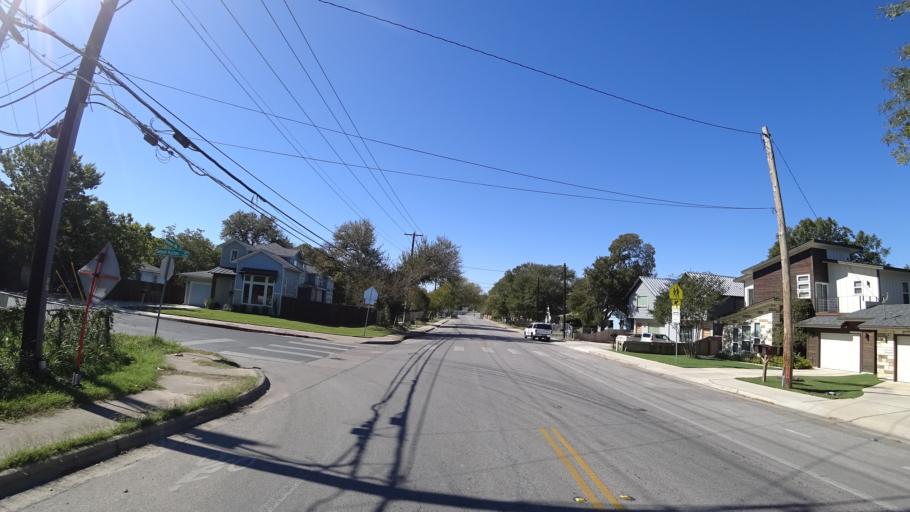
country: US
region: Texas
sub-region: Travis County
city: Austin
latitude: 30.2819
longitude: -97.6775
